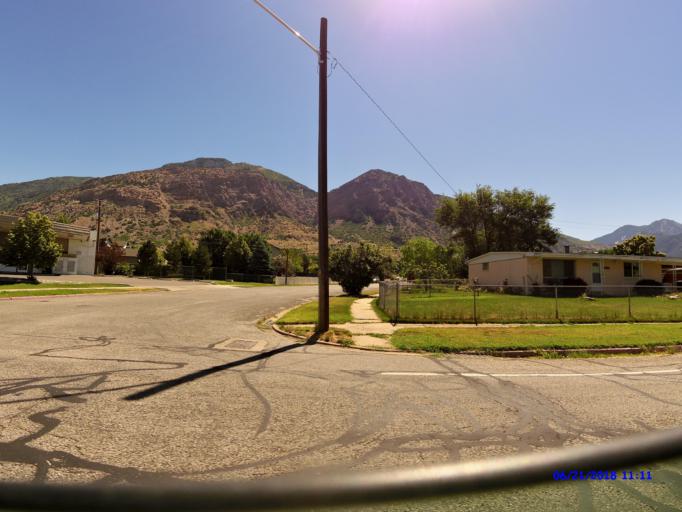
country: US
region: Utah
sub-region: Weber County
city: Harrisville
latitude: 41.2705
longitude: -111.9591
